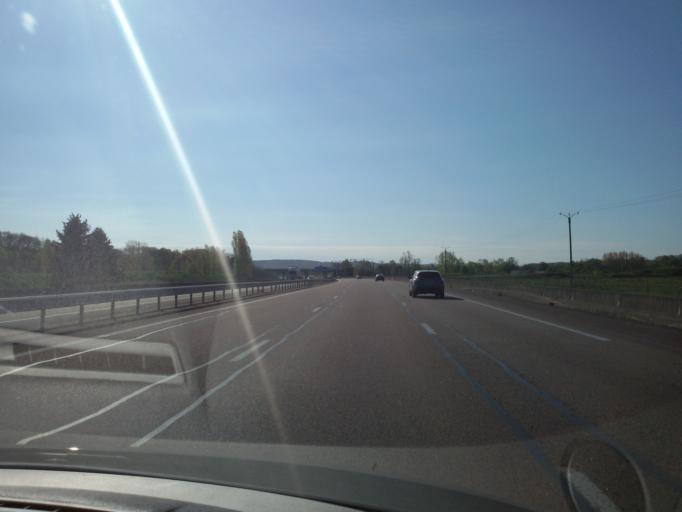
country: FR
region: Bourgogne
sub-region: Departement de l'Yonne
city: Appoigny
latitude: 47.8591
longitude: 3.5378
